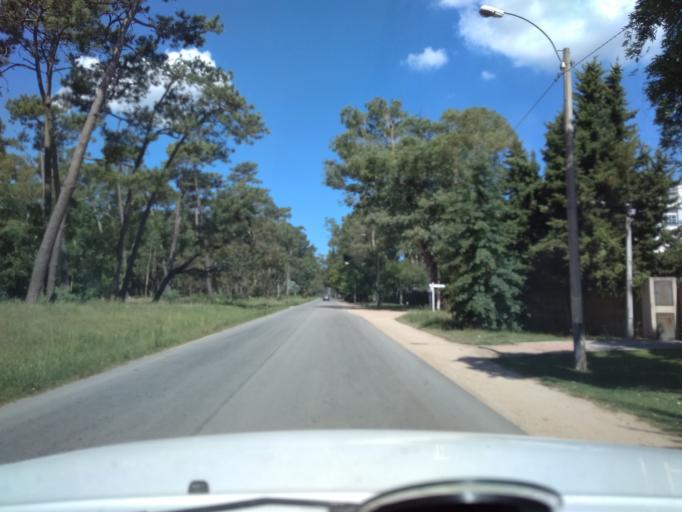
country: UY
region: Canelones
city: Paso de Carrasco
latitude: -34.8552
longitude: -56.0356
